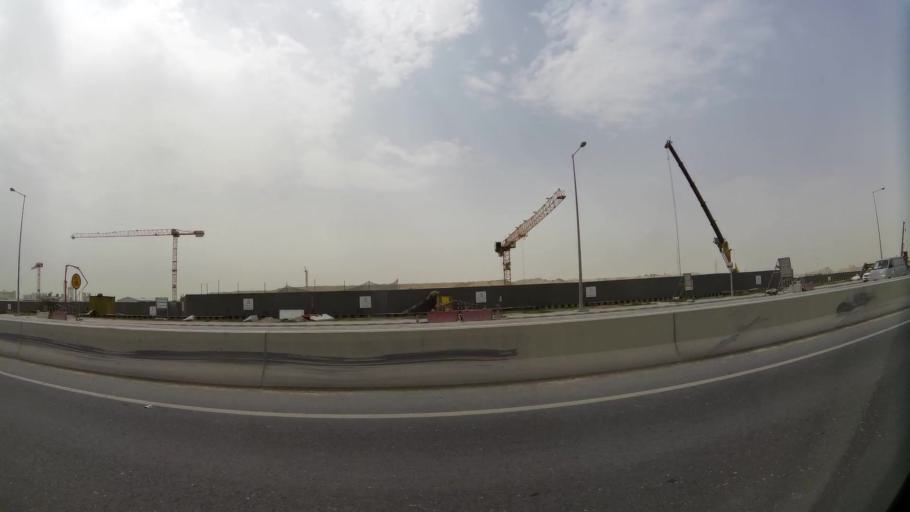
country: QA
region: Baladiyat ad Dawhah
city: Doha
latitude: 25.2946
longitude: 51.4834
